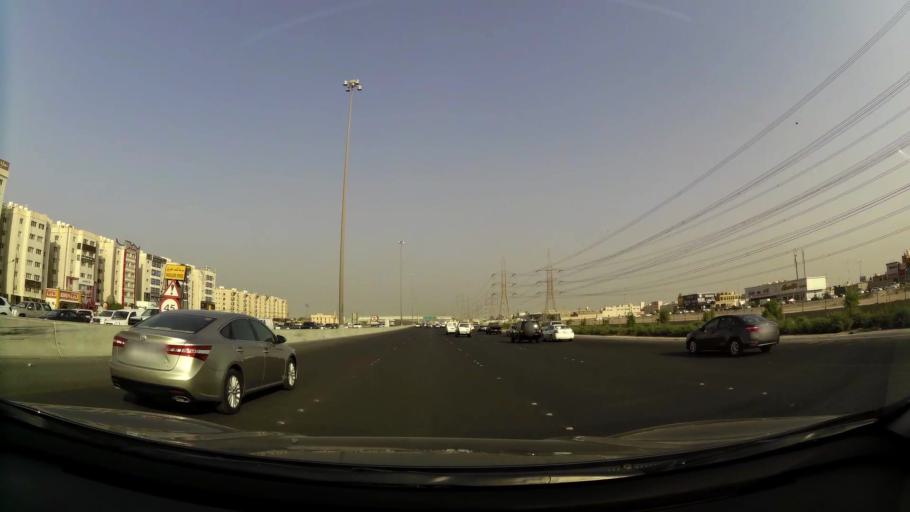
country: KW
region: Al Asimah
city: Ar Rabiyah
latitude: 29.2991
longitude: 47.9128
